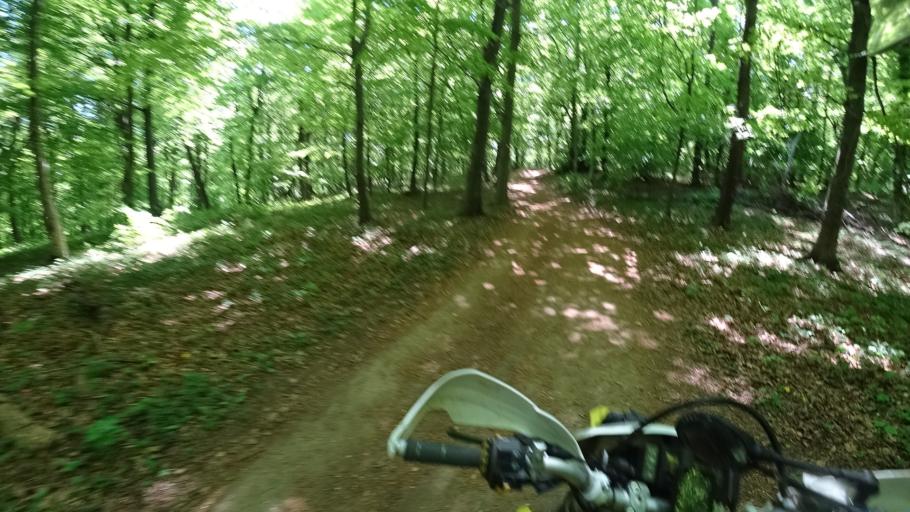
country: HR
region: Zagrebacka
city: Jablanovec
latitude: 45.8632
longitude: 15.8688
